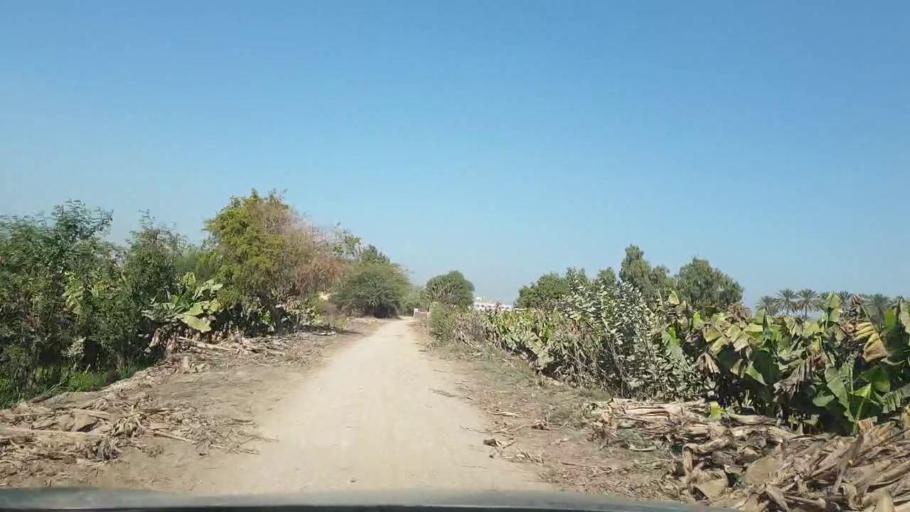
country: PK
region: Sindh
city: Tando Adam
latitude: 25.6358
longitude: 68.6753
